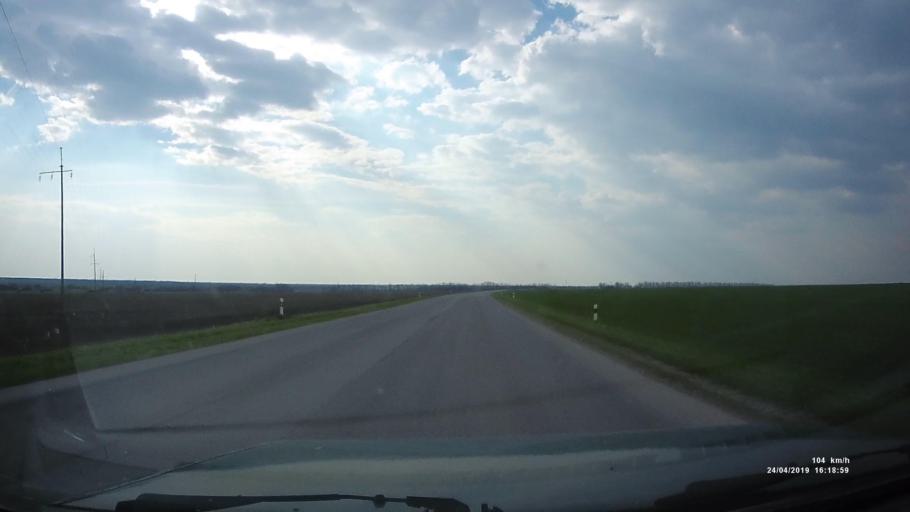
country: RU
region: Rostov
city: Sovetskoye
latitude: 46.7775
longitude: 42.1046
